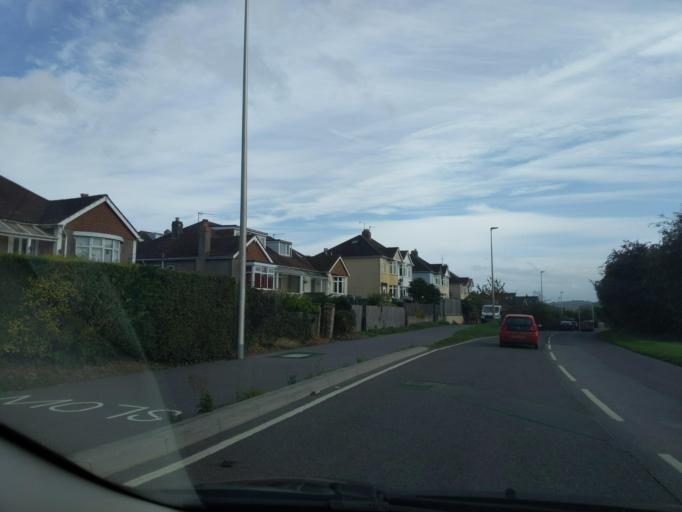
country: GB
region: England
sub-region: Devon
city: Newton Abbot
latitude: 50.5355
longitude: -3.6362
